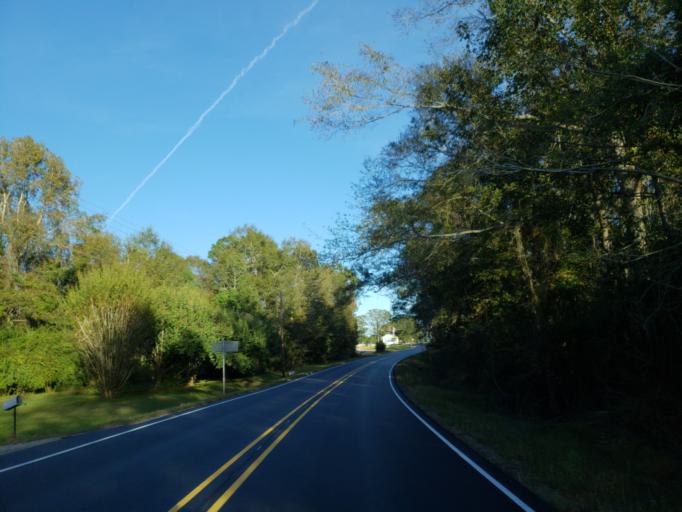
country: US
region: Mississippi
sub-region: Perry County
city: Richton
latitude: 31.3470
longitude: -88.7671
